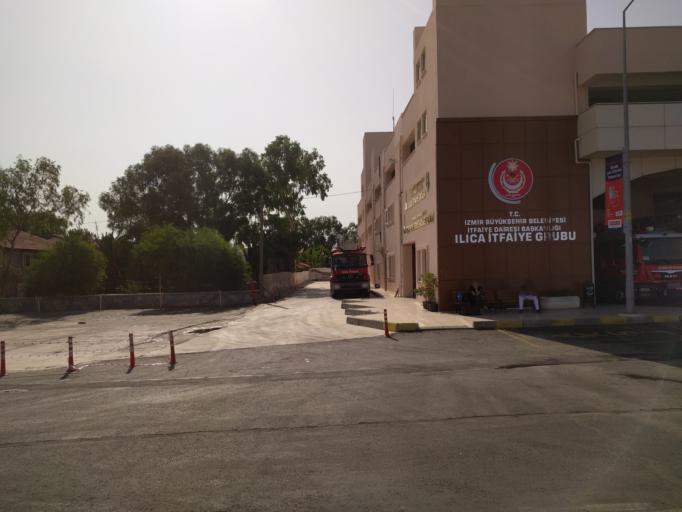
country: TR
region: Izmir
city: Alacati
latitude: 38.3054
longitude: 26.3626
